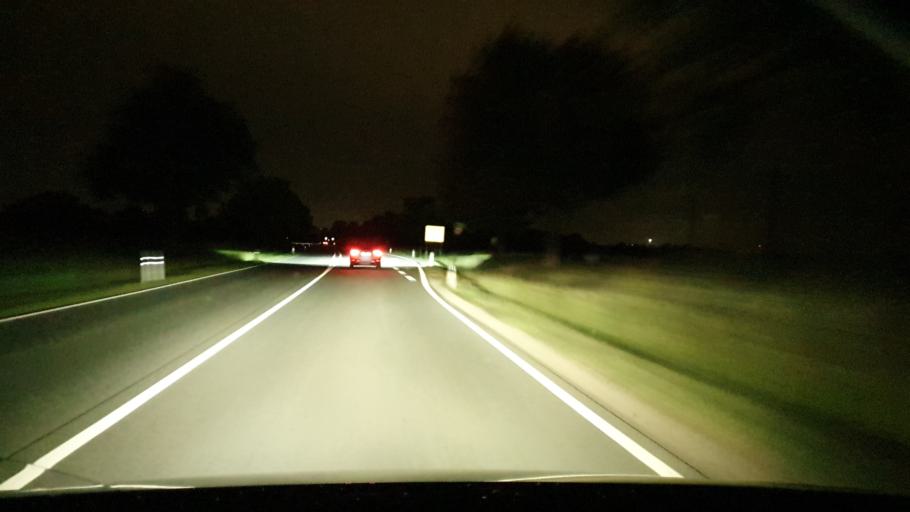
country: DE
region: Hesse
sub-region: Regierungsbezirk Darmstadt
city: Hochheim am Main
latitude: 50.0250
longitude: 8.3572
